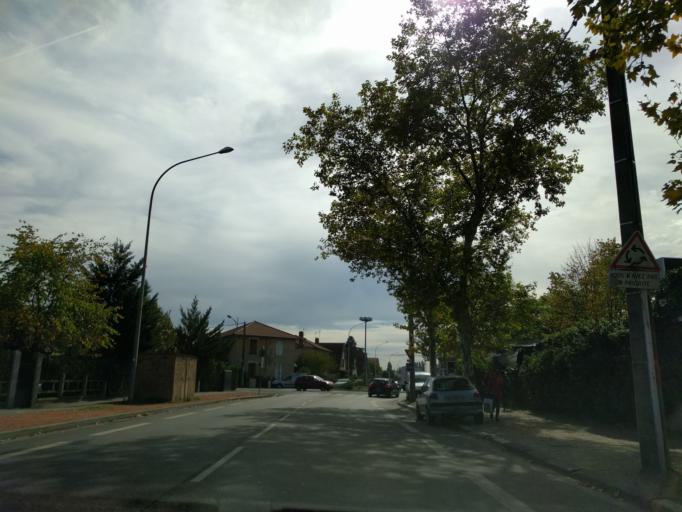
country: FR
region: Rhone-Alpes
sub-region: Departement du Rhone
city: Vaulx-en-Velin
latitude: 45.7586
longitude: 4.9211
